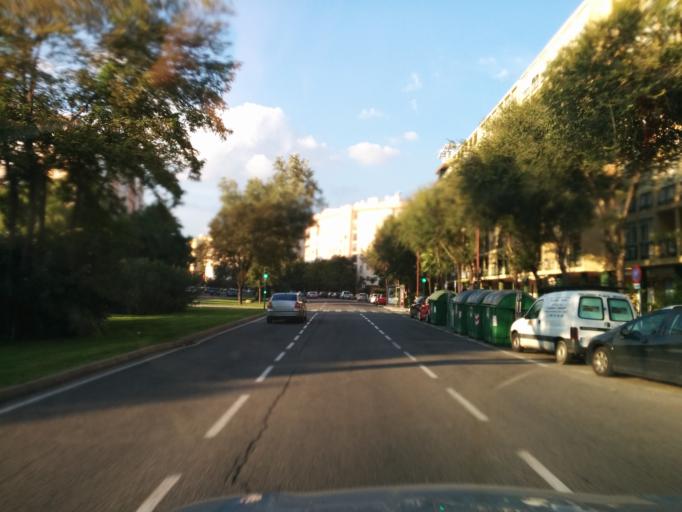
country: ES
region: Andalusia
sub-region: Provincia de Sevilla
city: Sevilla
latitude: 37.3909
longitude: -5.9199
